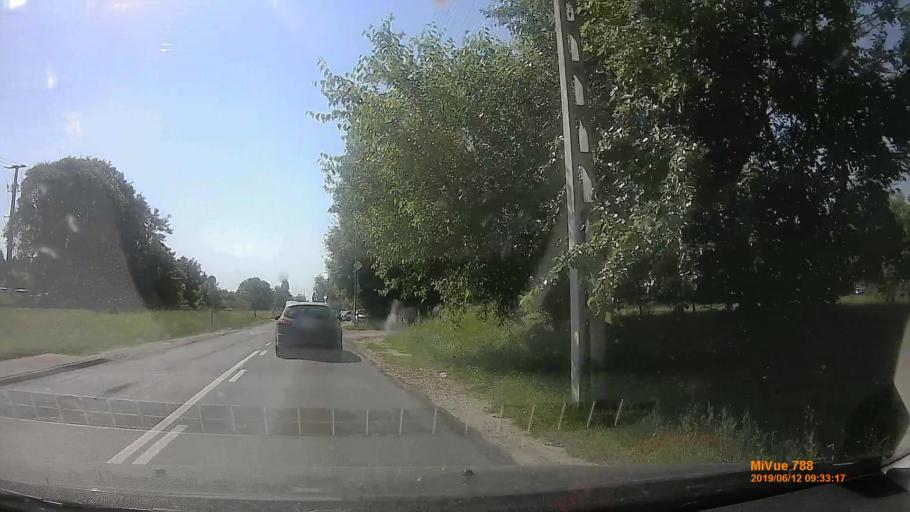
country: HU
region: Pest
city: Gyal
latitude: 47.3928
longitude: 19.2007
